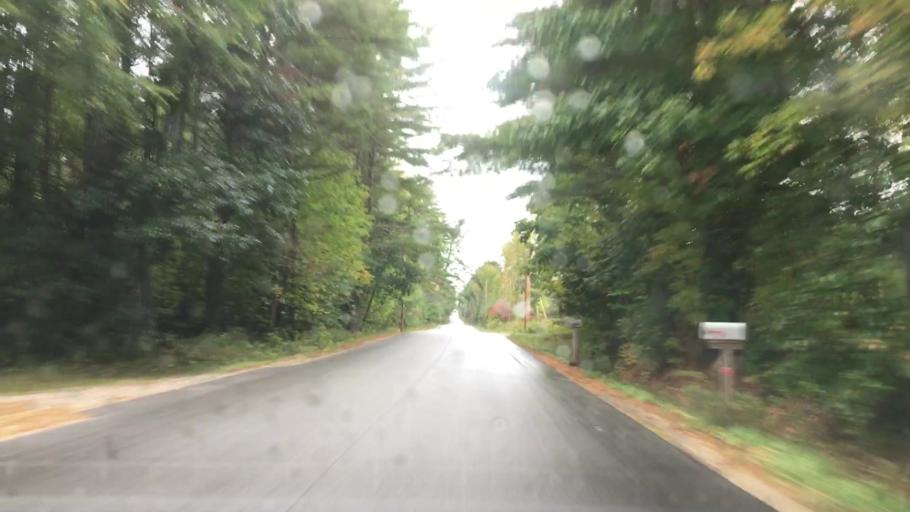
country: US
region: Maine
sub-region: Cumberland County
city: Harrison
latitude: 44.0870
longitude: -70.6499
